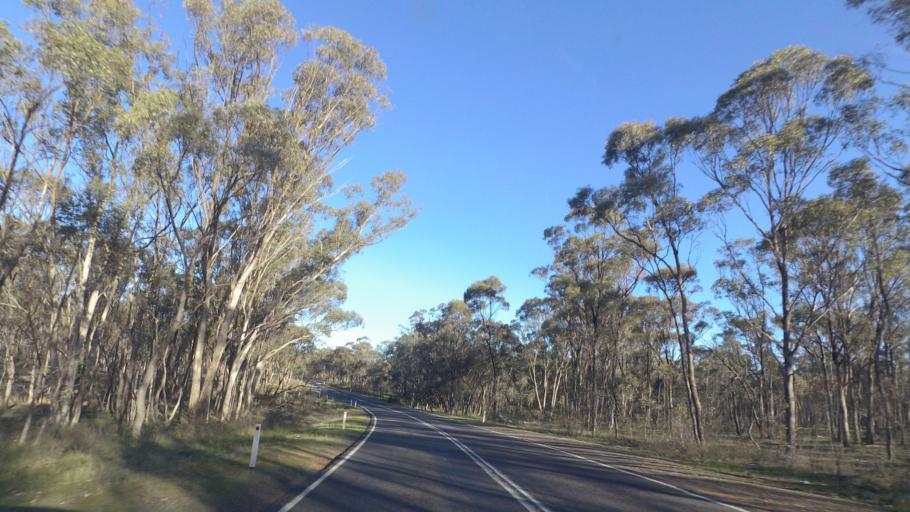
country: AU
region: Victoria
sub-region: Greater Bendigo
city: Kennington
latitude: -36.8907
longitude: 144.4932
